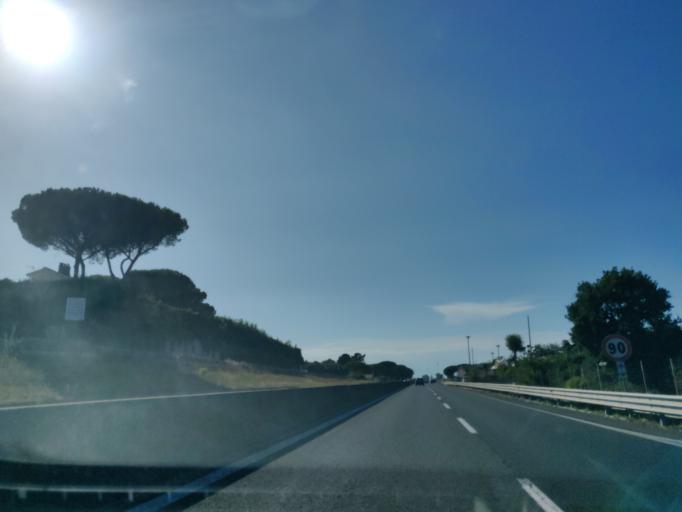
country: IT
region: Latium
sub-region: Citta metropolitana di Roma Capitale
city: Ara Nova
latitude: 41.9135
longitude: 12.2468
